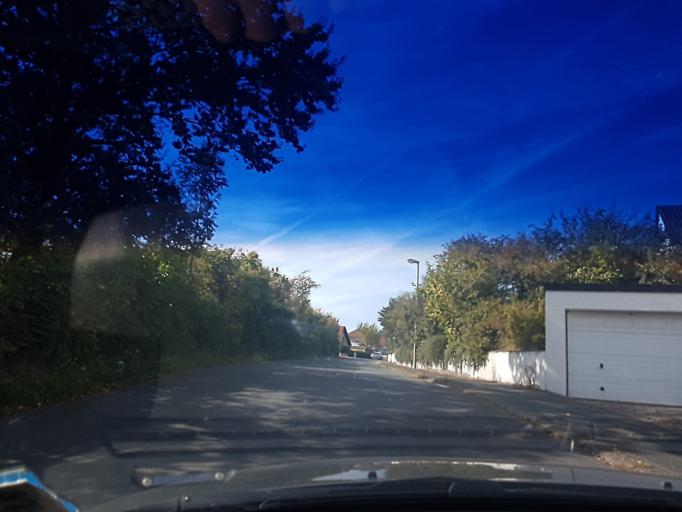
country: DE
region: Bavaria
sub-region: Upper Franconia
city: Schlusselfeld
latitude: 49.7637
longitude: 10.6200
